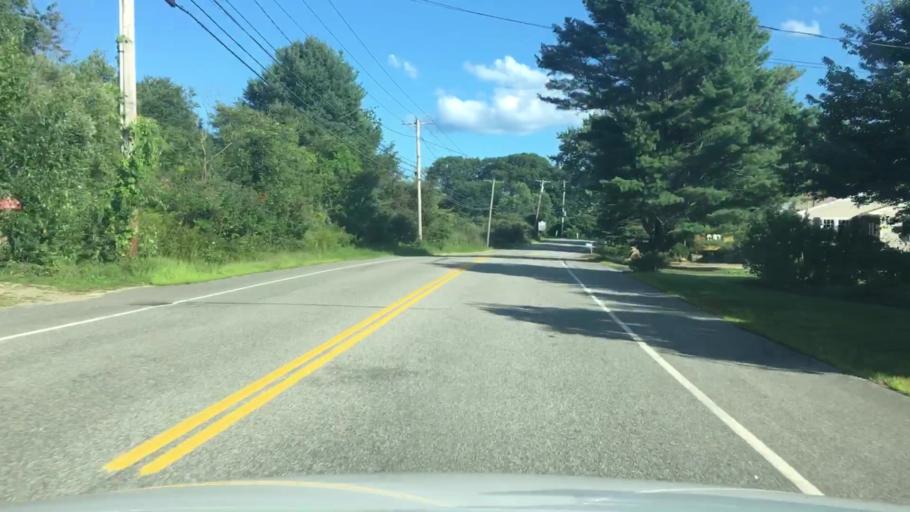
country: US
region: Maine
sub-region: Cumberland County
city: Scarborough
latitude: 43.5600
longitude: -70.3057
